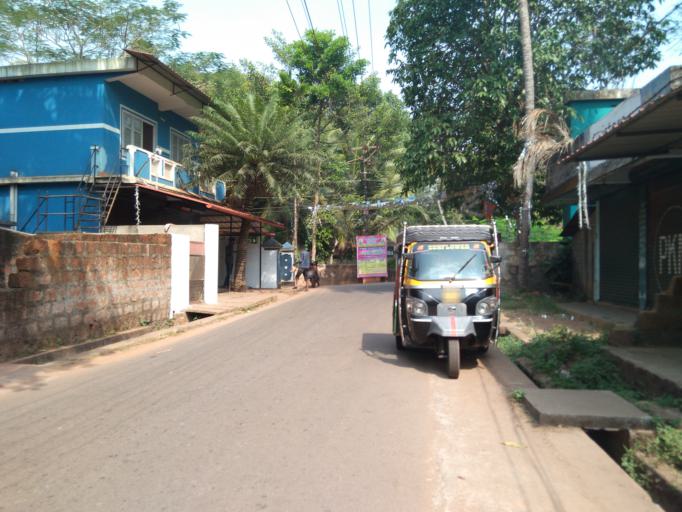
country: IN
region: Kerala
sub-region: Kozhikode
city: Kunnamangalam
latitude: 11.2918
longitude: 75.8363
